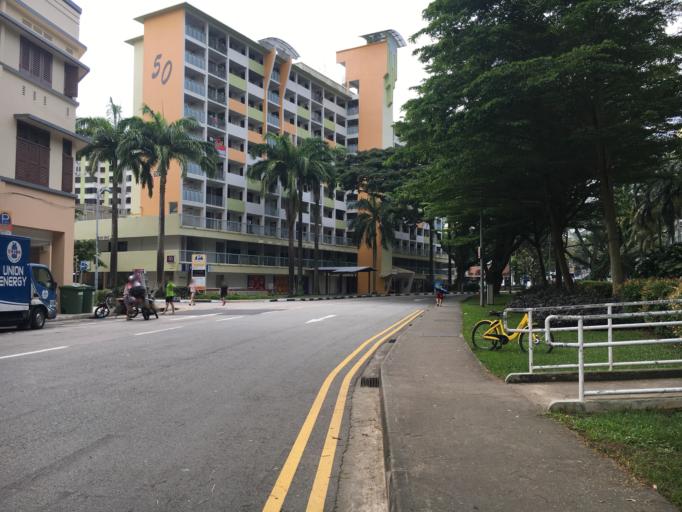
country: SG
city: Singapore
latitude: 1.2896
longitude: 103.8277
